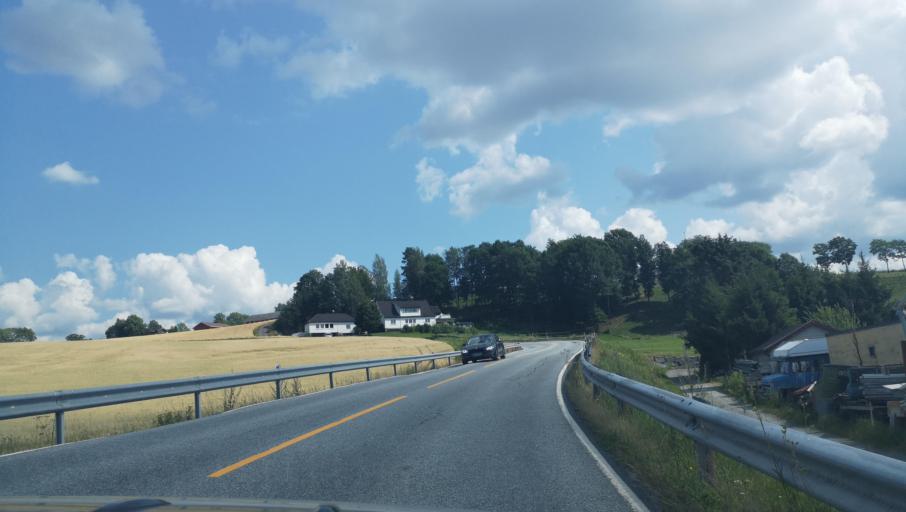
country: NO
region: Buskerud
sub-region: Ovre Eiker
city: Hokksund
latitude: 59.7261
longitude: 9.8350
